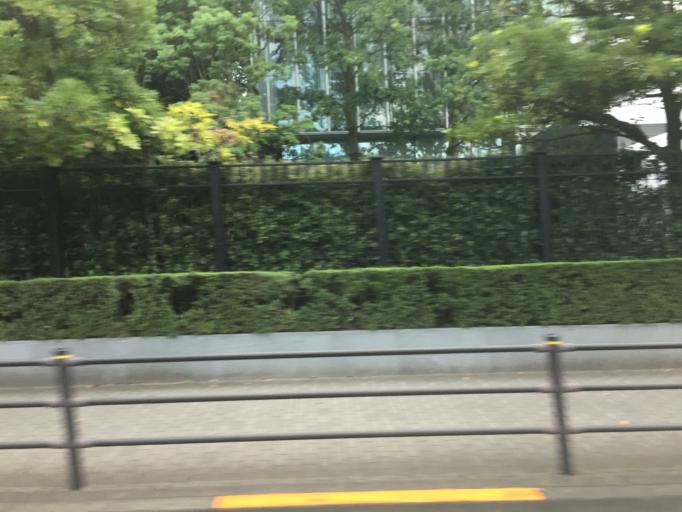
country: JP
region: Kanagawa
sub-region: Kawasaki-shi
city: Kawasaki
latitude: 35.5678
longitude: 139.6833
